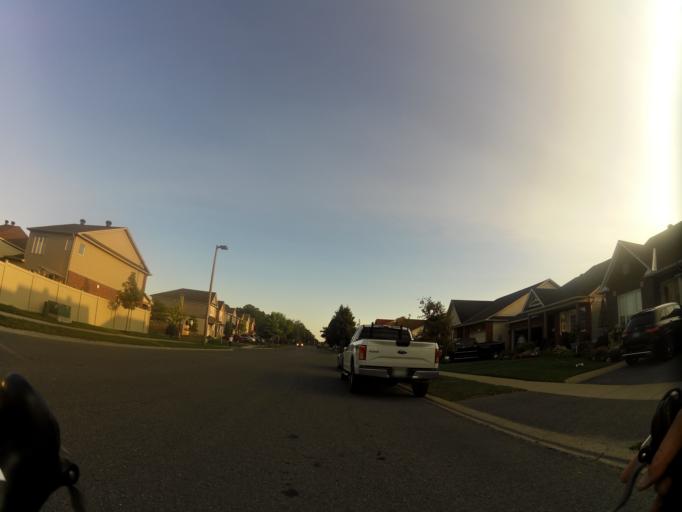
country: CA
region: Ontario
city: Bells Corners
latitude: 45.3507
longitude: -75.9331
